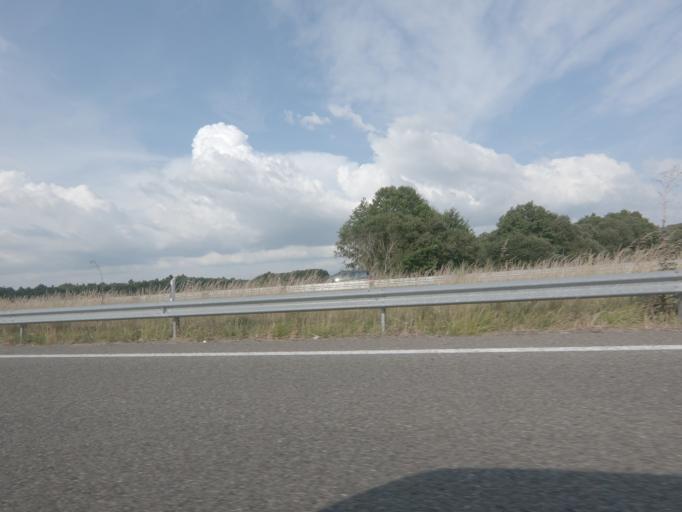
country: ES
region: Galicia
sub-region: Provincia de Ourense
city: Xinzo de Limia
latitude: 42.1323
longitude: -7.7422
